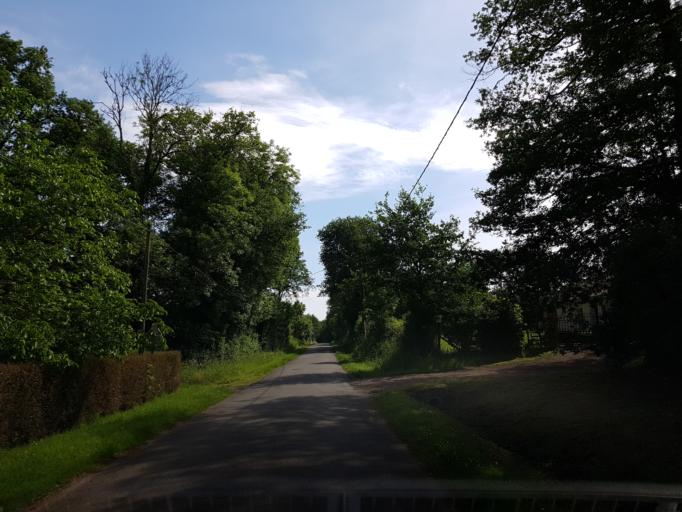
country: FR
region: Poitou-Charentes
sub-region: Departement de la Charente
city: Chabanais
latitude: 45.9221
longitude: 0.7140
